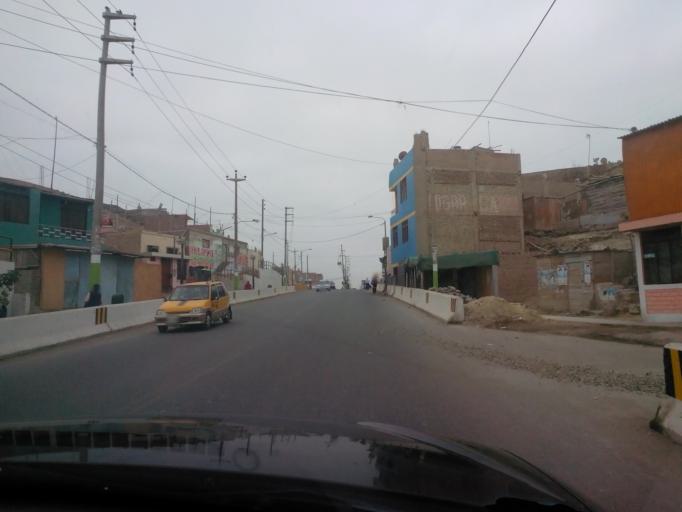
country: PE
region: Ica
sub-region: Provincia de Pisco
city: San Clemente
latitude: -13.6828
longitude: -76.1584
